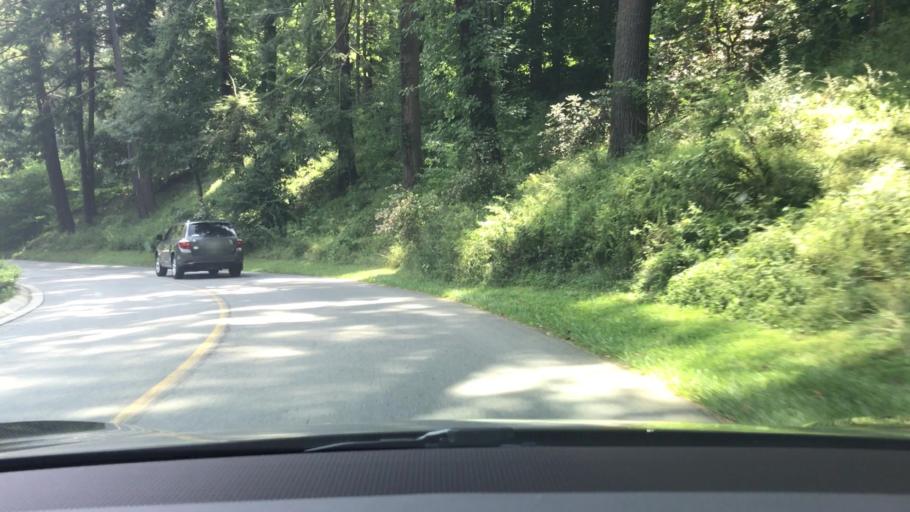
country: US
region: North Carolina
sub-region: Buncombe County
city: Asheville
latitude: 35.5634
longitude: -82.5516
